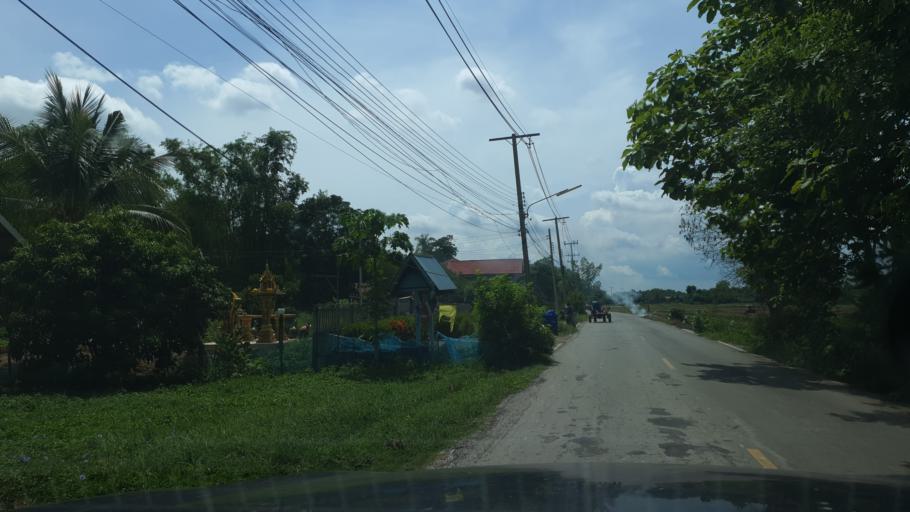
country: TH
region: Sukhothai
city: Sukhothai
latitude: 16.9958
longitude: 99.8577
